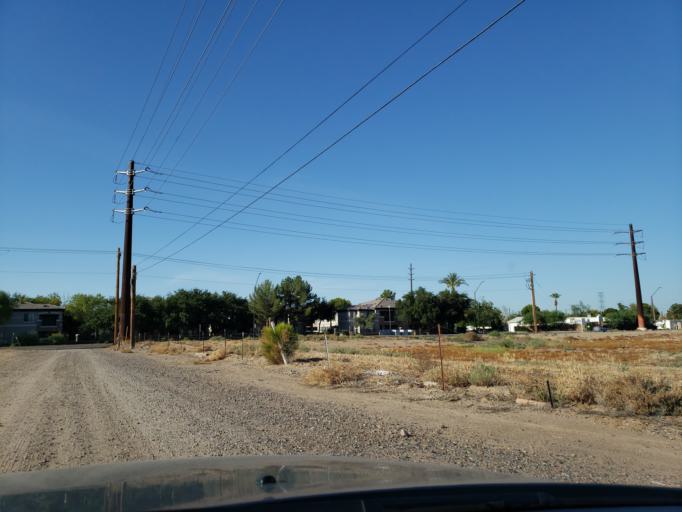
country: US
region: Arizona
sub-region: Maricopa County
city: Avondale
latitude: 33.4648
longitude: -112.3142
